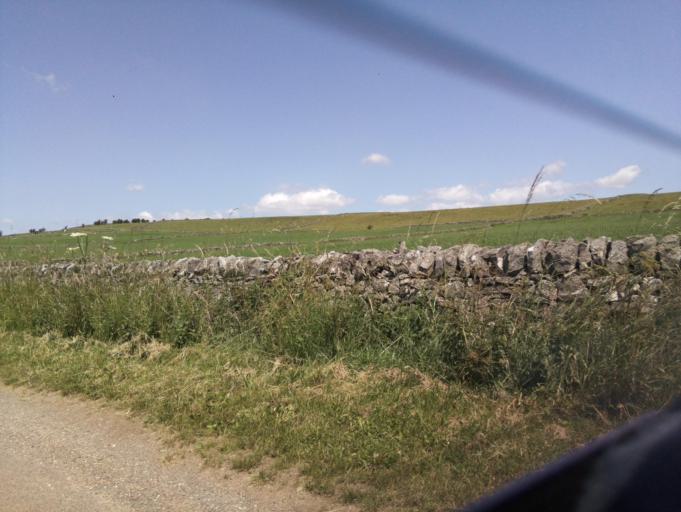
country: GB
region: England
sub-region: Derbyshire
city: Buxton
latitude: 53.2796
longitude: -1.8473
